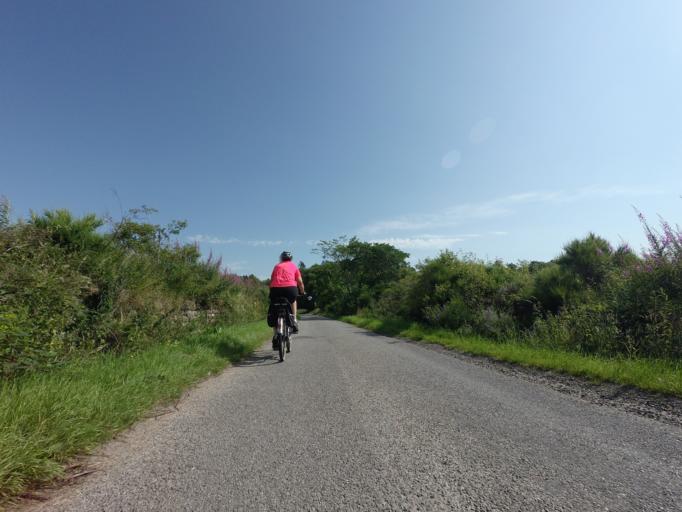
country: GB
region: Scotland
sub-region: Highland
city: Alness
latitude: 57.7146
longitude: -4.2182
